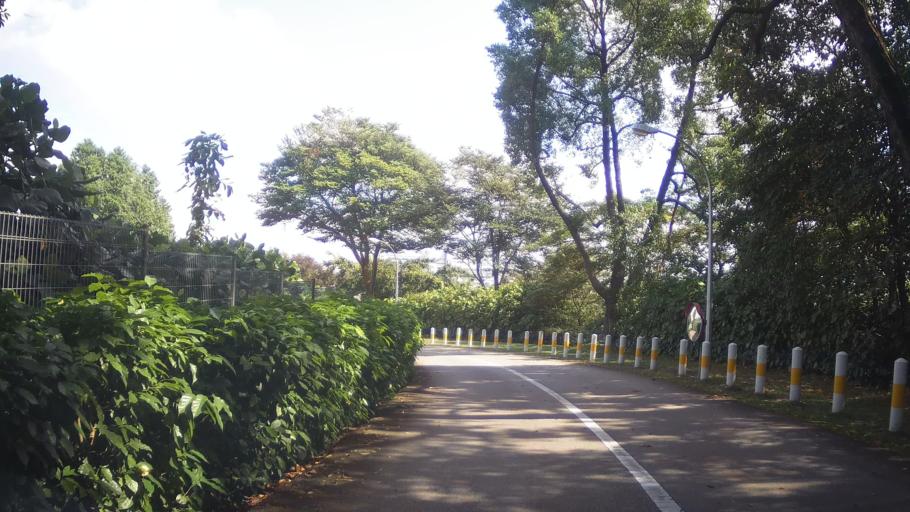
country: SG
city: Singapore
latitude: 1.3189
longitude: 103.7092
